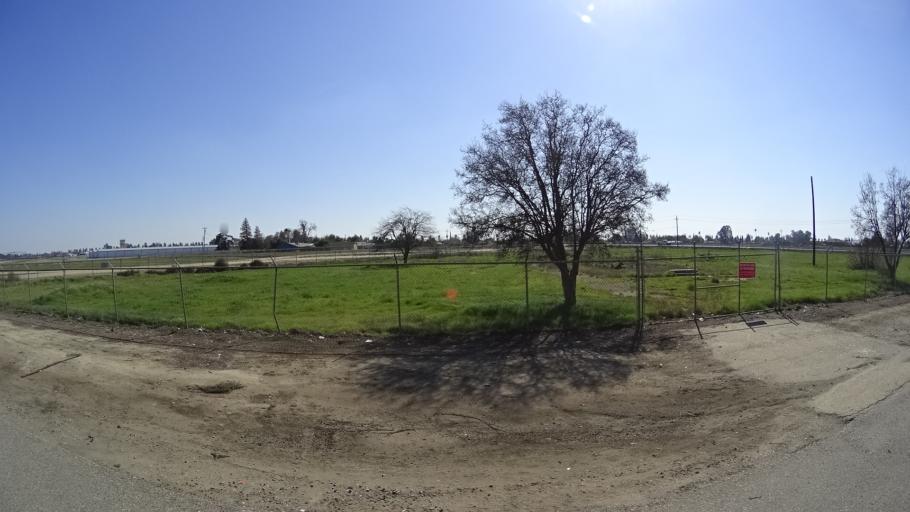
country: US
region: California
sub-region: Fresno County
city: West Park
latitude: 36.7357
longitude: -119.8278
